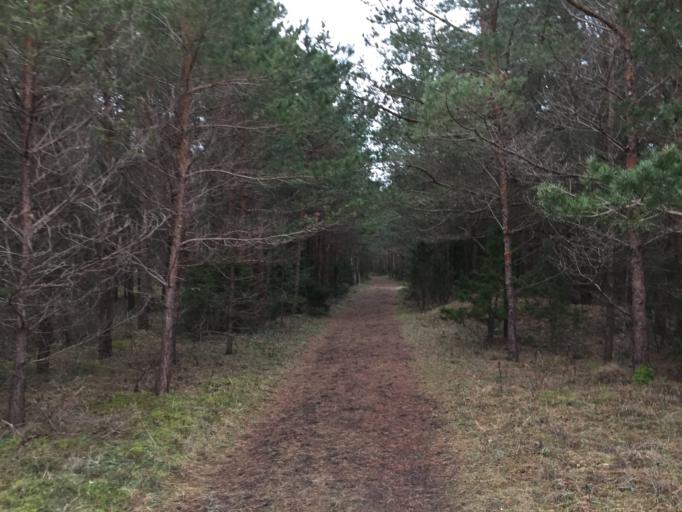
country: EE
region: Saare
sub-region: Kuressaare linn
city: Kuressaare
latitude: 58.5689
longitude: 22.2867
